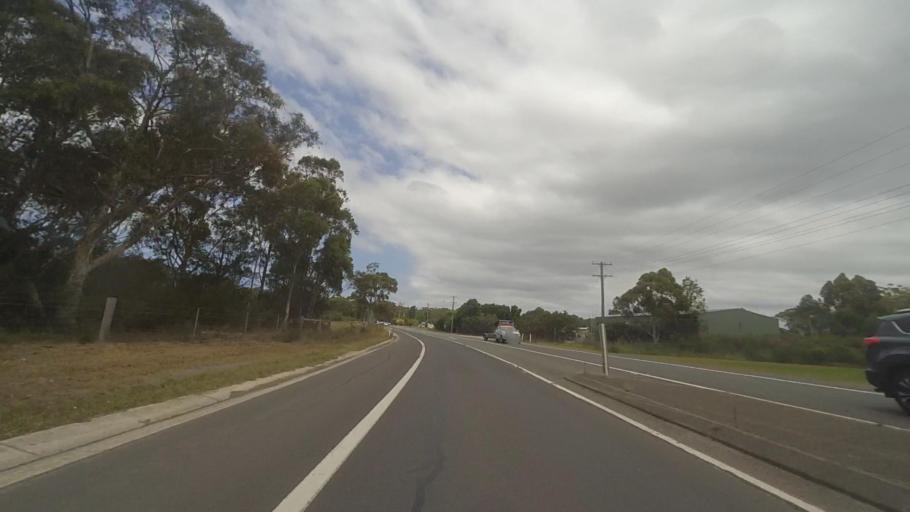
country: AU
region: New South Wales
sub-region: Shoalhaven Shire
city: Falls Creek
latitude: -35.0920
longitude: 150.5075
